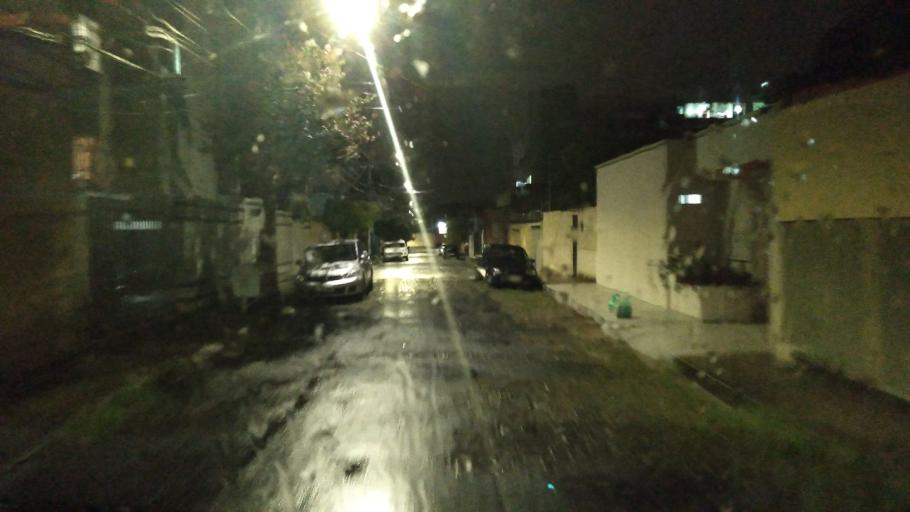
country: BR
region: Minas Gerais
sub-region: Belo Horizonte
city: Belo Horizonte
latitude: -19.9093
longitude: -43.9785
